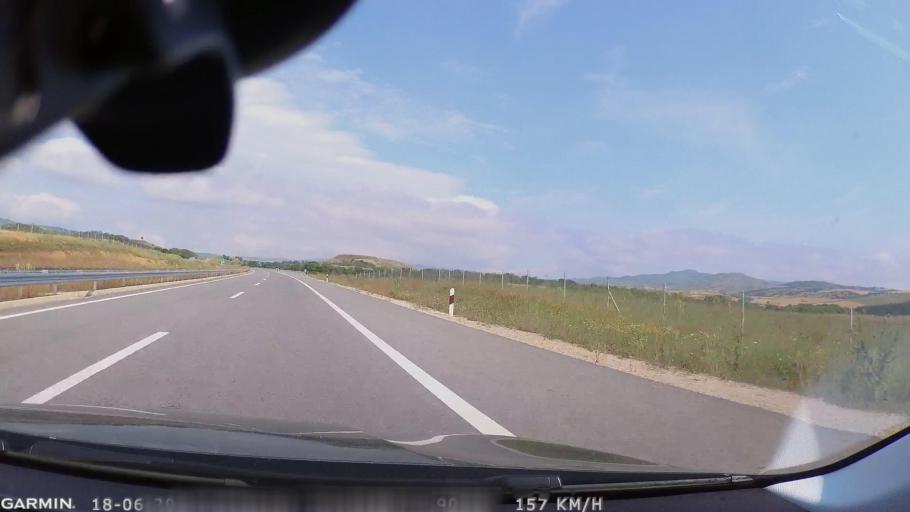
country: MK
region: Sveti Nikole
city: Gorobinci
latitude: 41.9112
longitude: 21.8992
